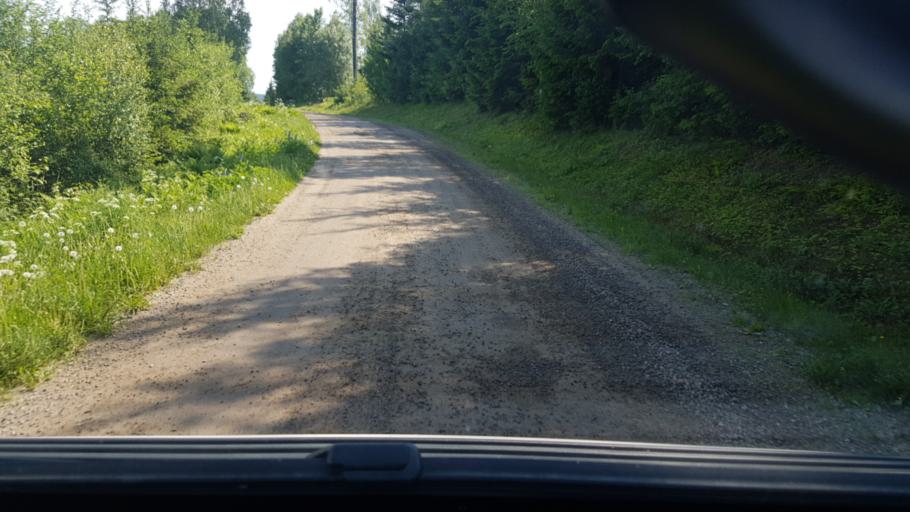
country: SE
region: Vaermland
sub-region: Eda Kommun
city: Amotfors
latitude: 59.7933
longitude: 12.4262
